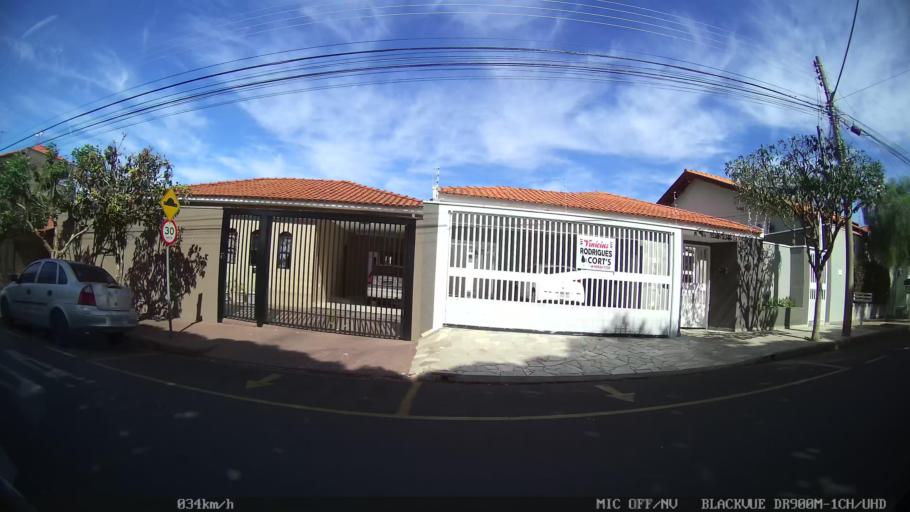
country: BR
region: Sao Paulo
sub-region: Sao Jose Do Rio Preto
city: Sao Jose do Rio Preto
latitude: -20.8440
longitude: -49.3663
